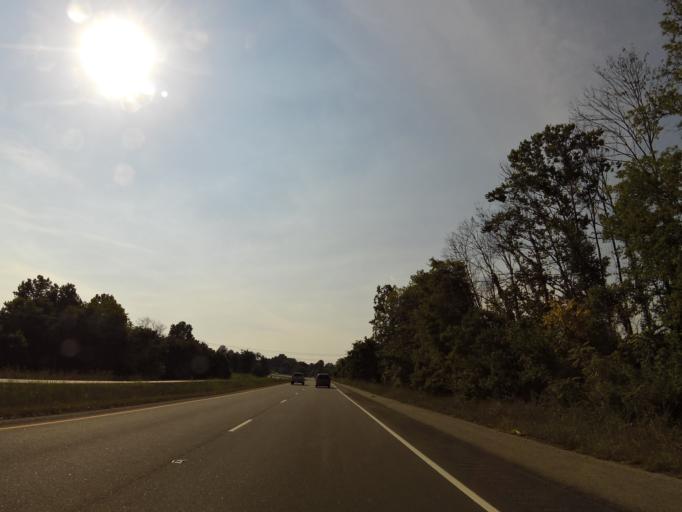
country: US
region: Tennessee
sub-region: Loudon County
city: Greenback
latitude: 35.7539
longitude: -84.1275
